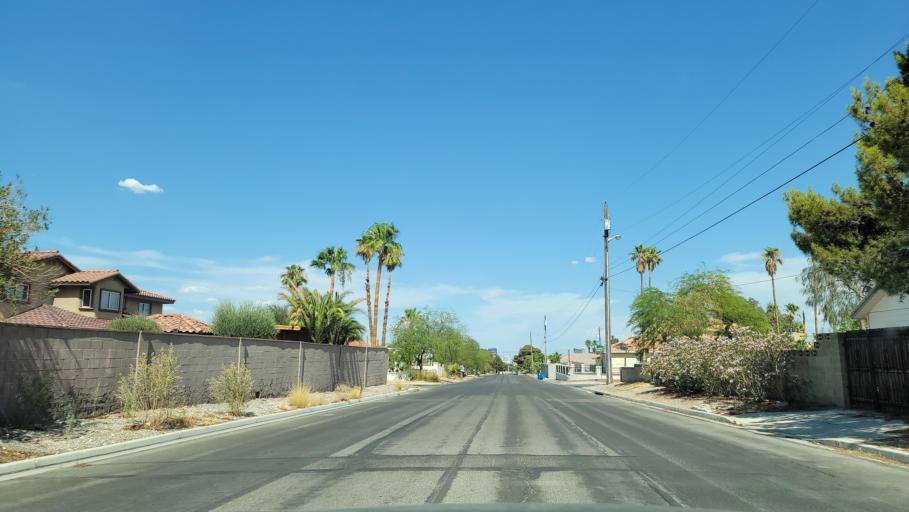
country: US
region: Nevada
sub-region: Clark County
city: Spring Valley
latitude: 36.1349
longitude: -115.2483
